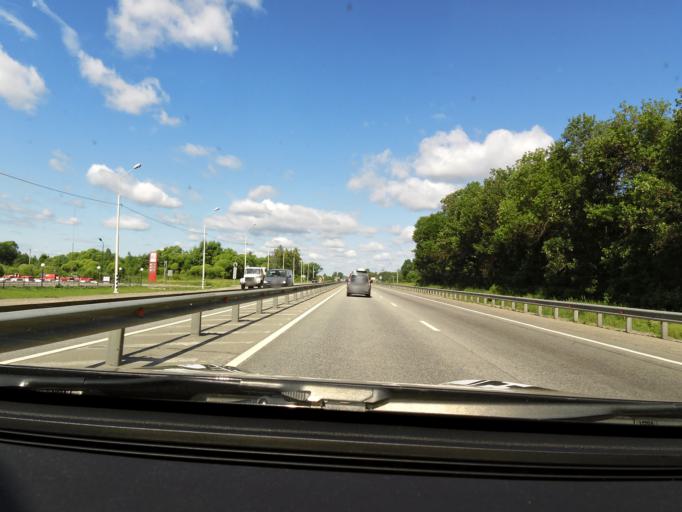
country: RU
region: Tverskaya
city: Likhoslavl'
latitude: 56.9734
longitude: 35.2885
